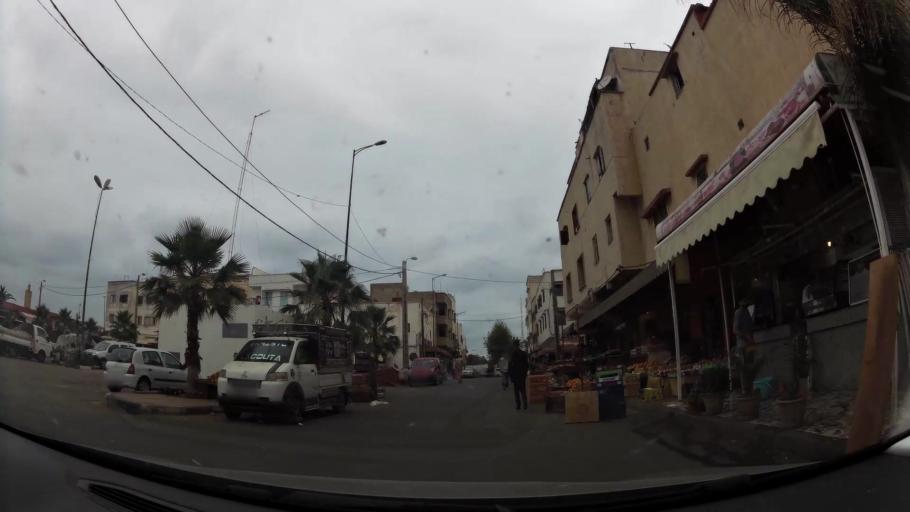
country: MA
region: Rabat-Sale-Zemmour-Zaer
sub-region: Rabat
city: Rabat
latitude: 34.0086
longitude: -6.8596
